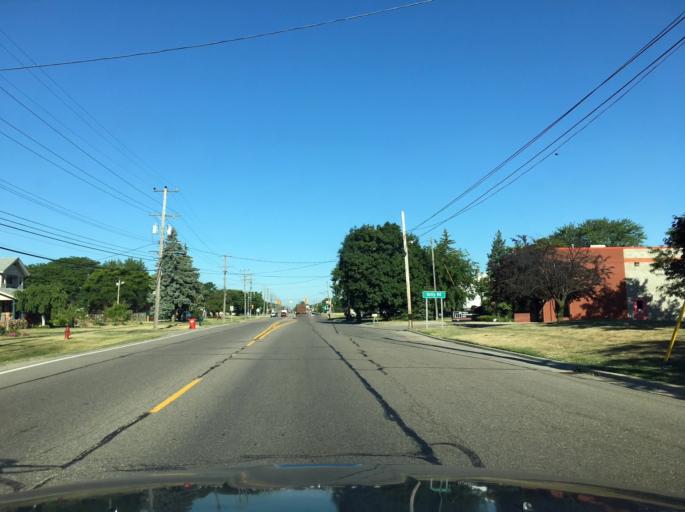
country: US
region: Michigan
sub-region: Macomb County
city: Fraser
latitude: 42.5394
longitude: -82.9271
